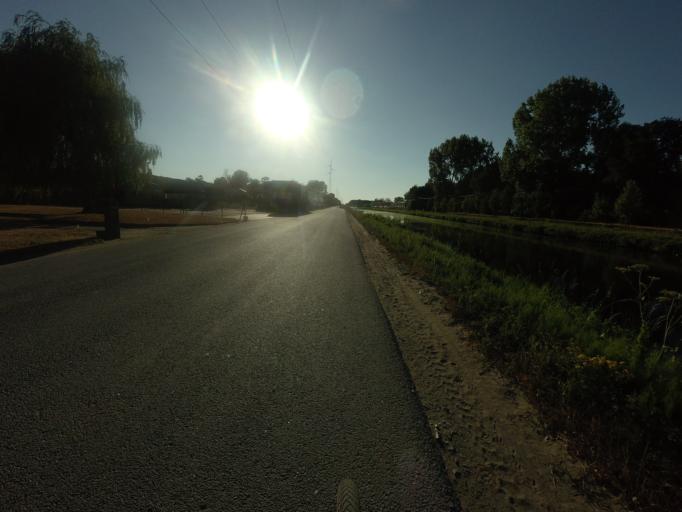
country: BE
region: Flanders
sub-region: Provincie Antwerpen
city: Rijkevorsel
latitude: 51.3333
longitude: 4.7331
